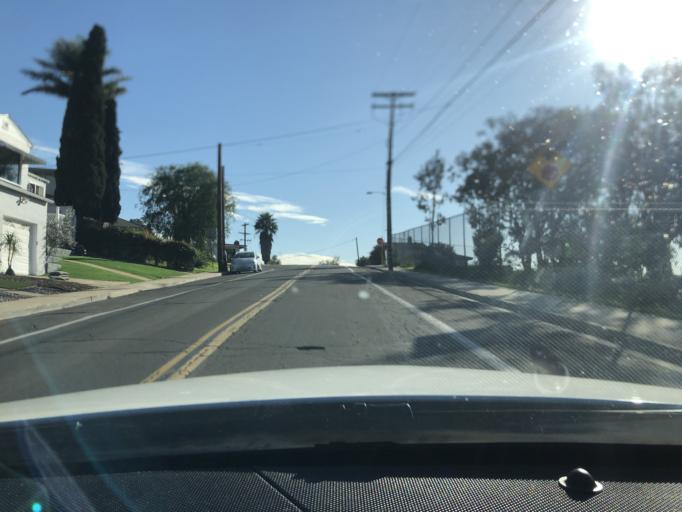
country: US
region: California
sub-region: San Diego County
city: Lemon Grove
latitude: 32.7557
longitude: -117.0729
